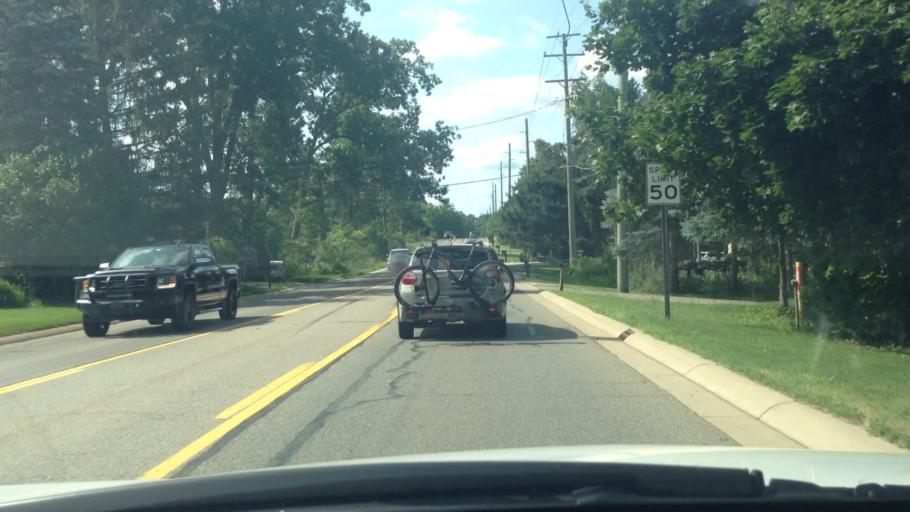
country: US
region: Michigan
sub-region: Oakland County
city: Wolverine Lake
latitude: 42.6229
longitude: -83.4423
